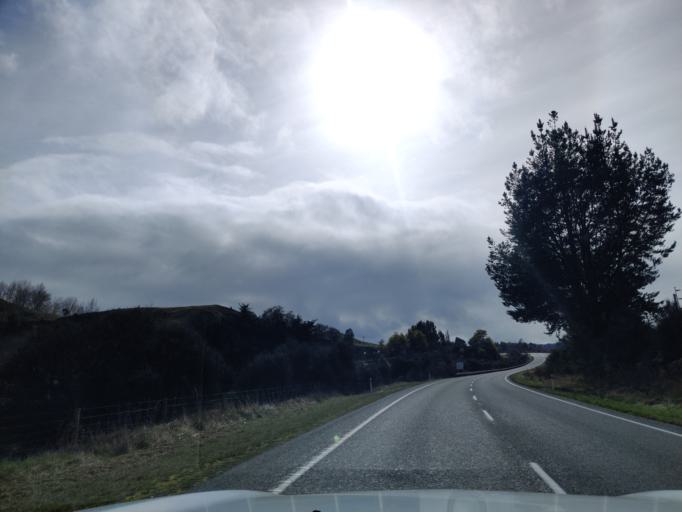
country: NZ
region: Manawatu-Wanganui
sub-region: Ruapehu District
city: Waiouru
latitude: -39.7555
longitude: 175.8299
